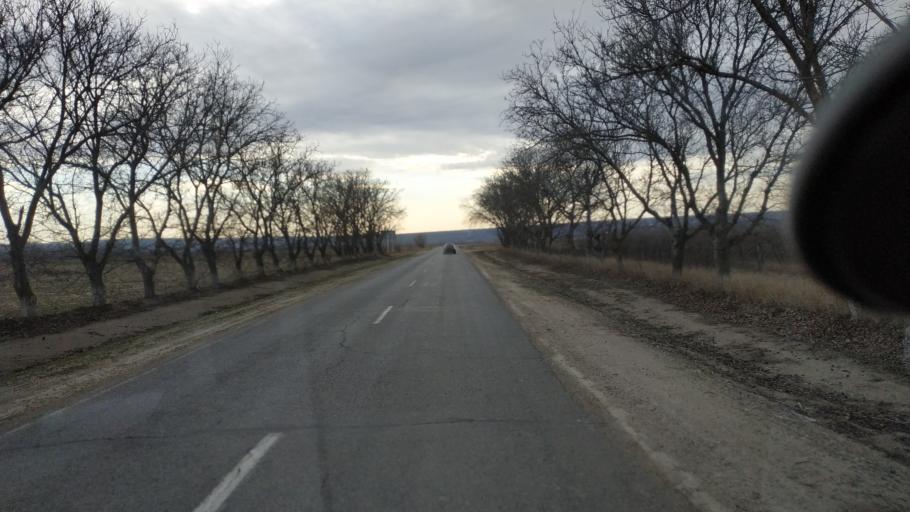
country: MD
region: Chisinau
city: Vadul lui Voda
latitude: 47.1553
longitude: 29.1051
